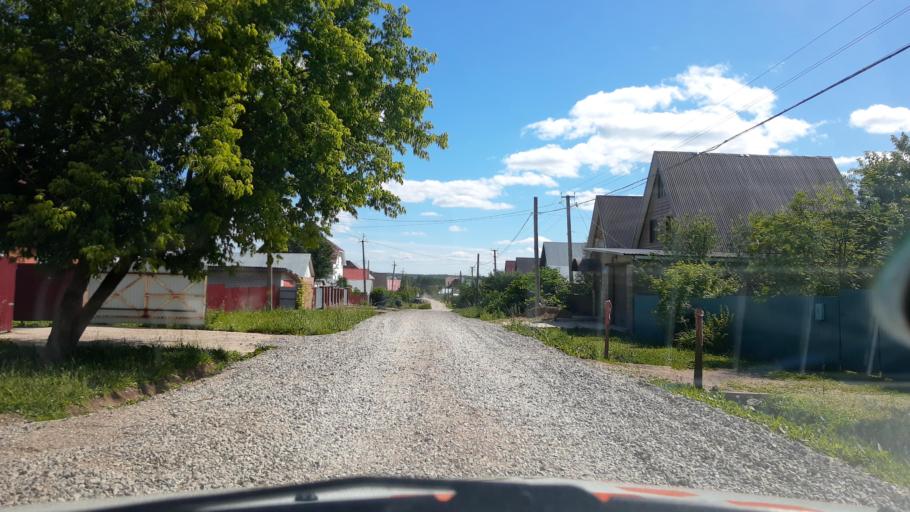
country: RU
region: Bashkortostan
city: Iglino
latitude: 54.8481
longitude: 56.4231
